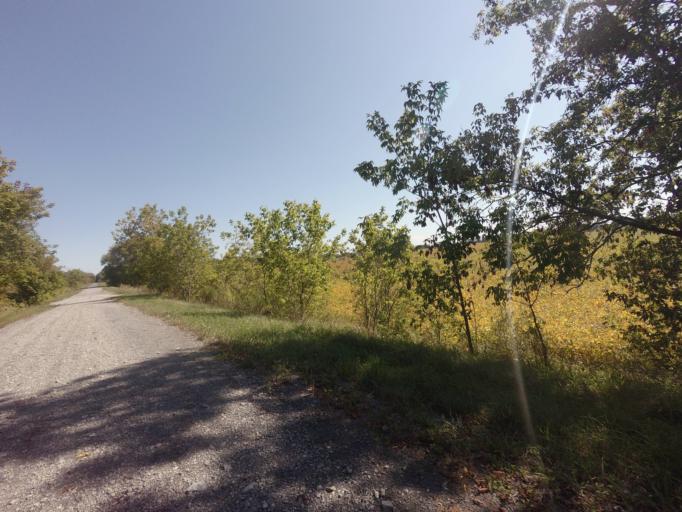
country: CA
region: Ontario
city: Bourget
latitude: 45.4544
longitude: -75.0908
